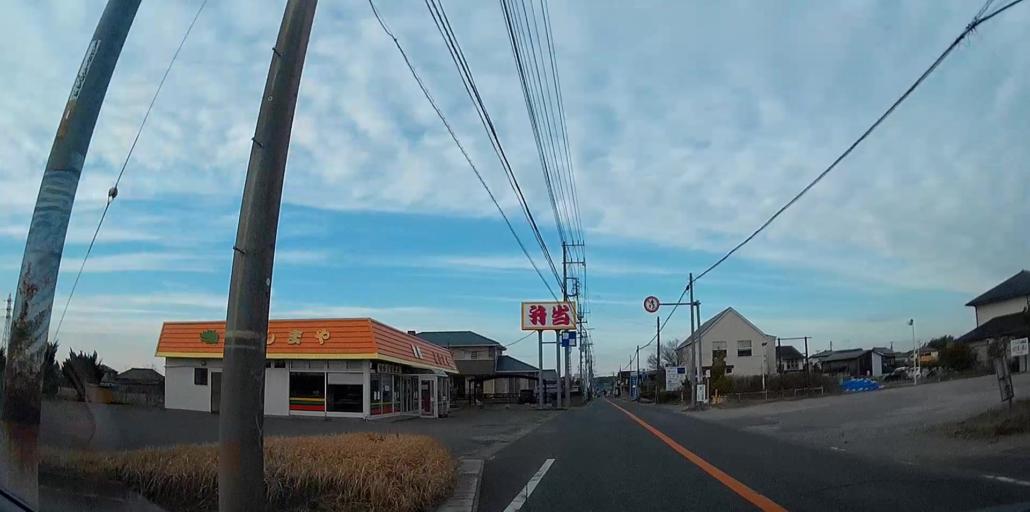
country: JP
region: Chiba
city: Kisarazu
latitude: 35.3608
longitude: 140.0576
